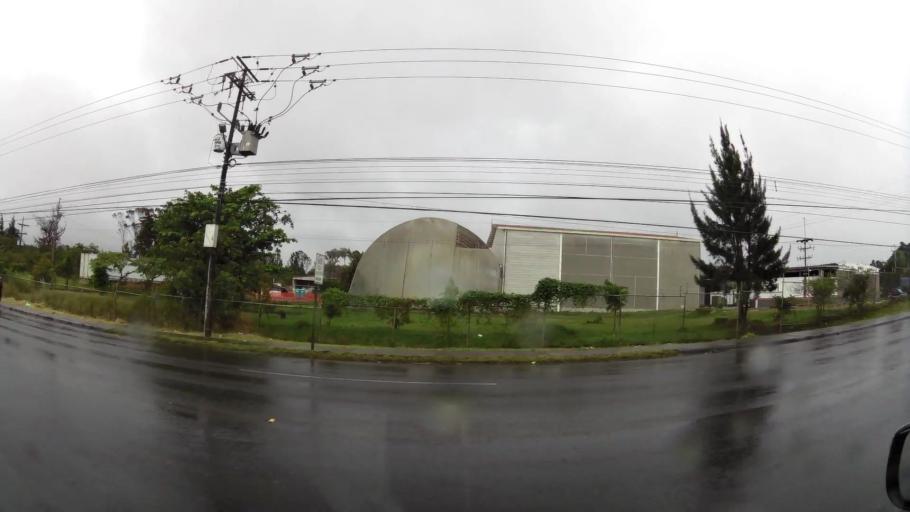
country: CR
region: Cartago
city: Paraiso
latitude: 9.8446
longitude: -83.8882
